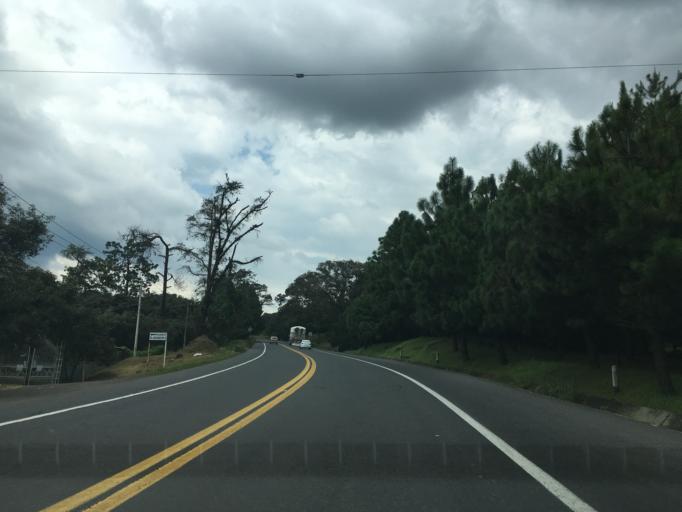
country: MX
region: Michoacan
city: Capacuaro
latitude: 19.5048
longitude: -102.0734
